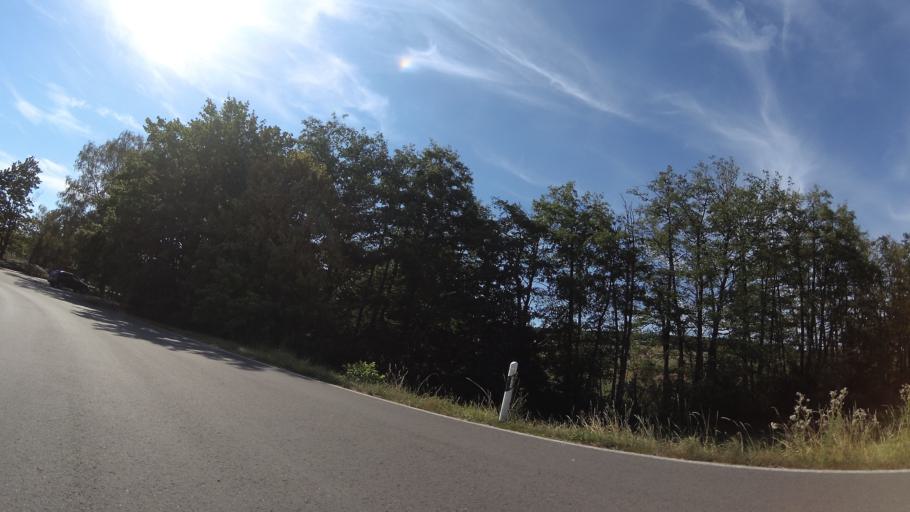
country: DE
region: Saarland
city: Blieskastel
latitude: 49.1694
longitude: 7.2911
